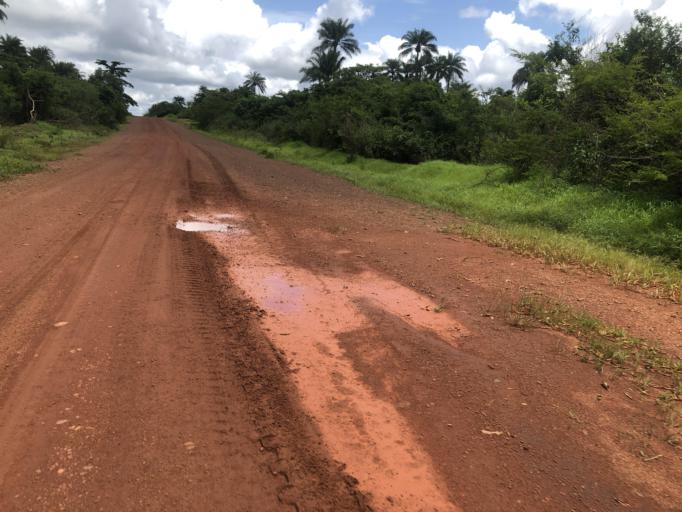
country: SL
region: Northern Province
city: Port Loko
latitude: 8.7178
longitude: -12.8399
